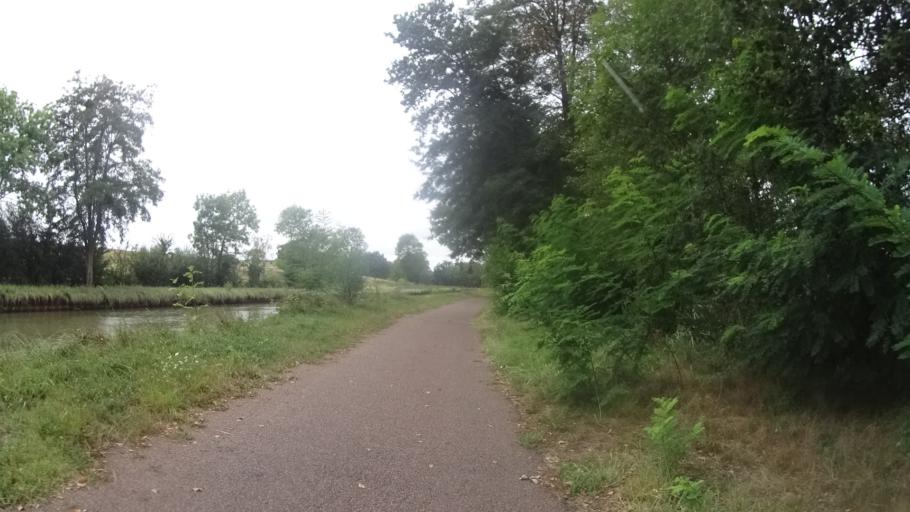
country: FR
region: Bourgogne
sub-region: Departement de la Nievre
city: Saint-Leger-des-Vignes
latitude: 46.8138
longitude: 3.3838
